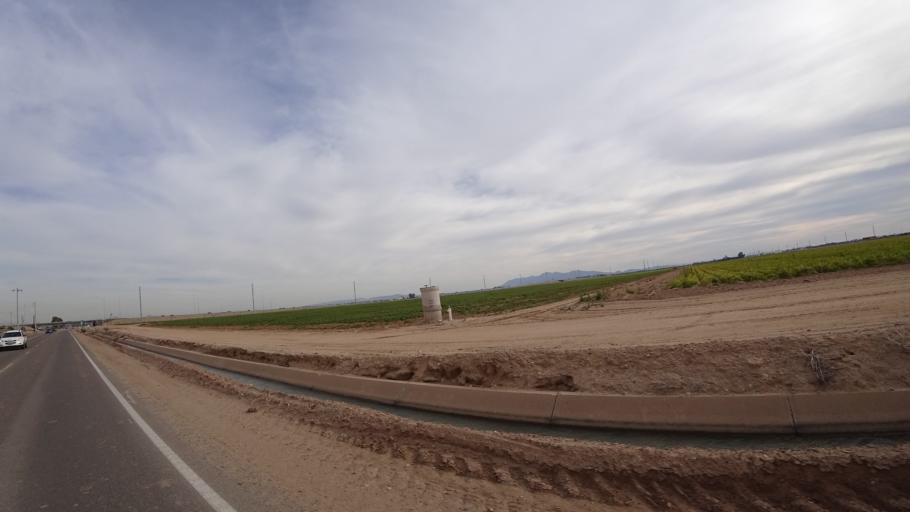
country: US
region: Arizona
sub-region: Maricopa County
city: Citrus Park
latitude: 33.5807
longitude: -112.4249
